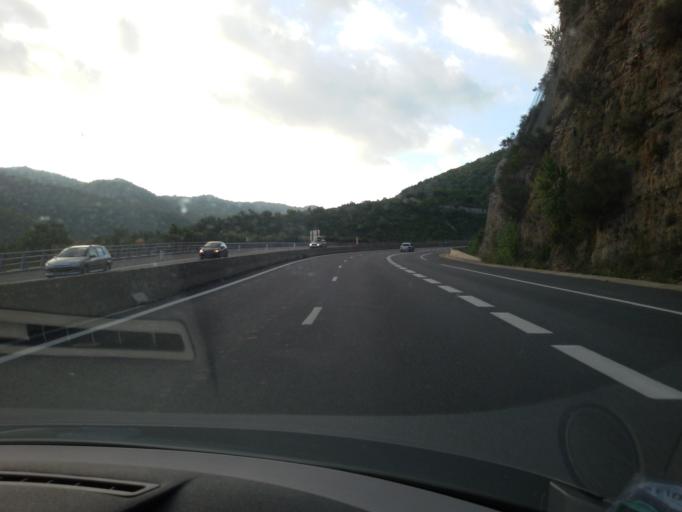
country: FR
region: Languedoc-Roussillon
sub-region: Departement de l'Herault
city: Lodeve
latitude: 43.8065
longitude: 3.3267
